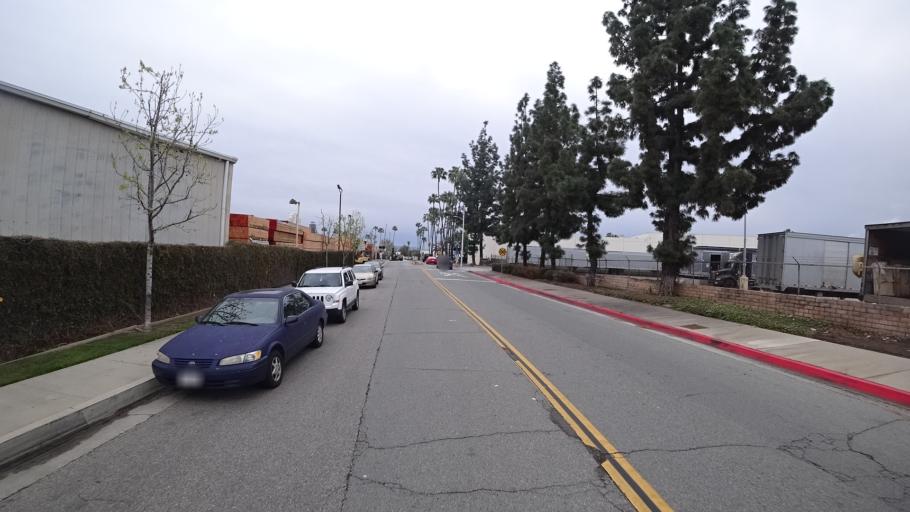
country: US
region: California
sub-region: Los Angeles County
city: West Puente Valley
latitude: 34.0650
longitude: -117.9811
